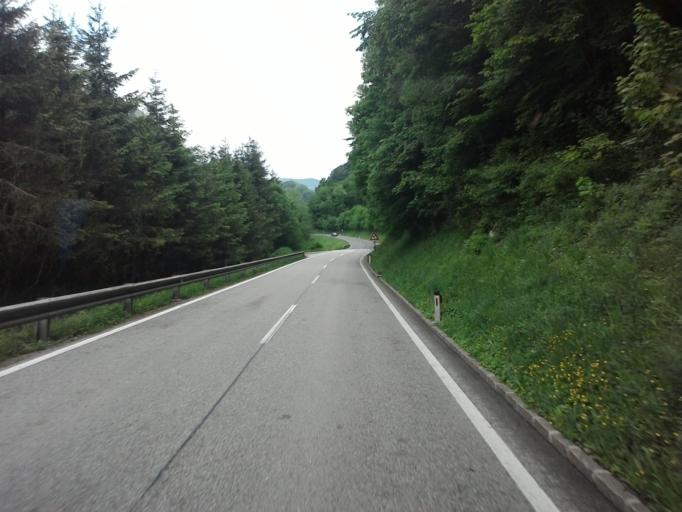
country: AT
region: Upper Austria
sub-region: Politischer Bezirk Steyr-Land
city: Weyer
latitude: 47.8583
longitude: 14.6164
